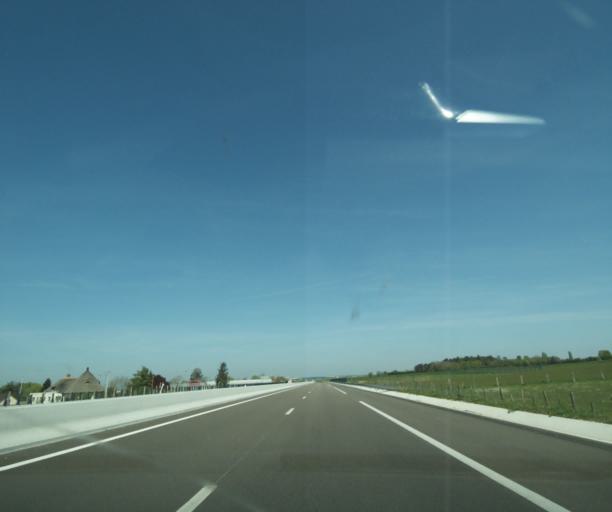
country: FR
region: Bourgogne
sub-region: Departement de la Nievre
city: Saint-Pierre-le-Moutier
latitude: 46.8113
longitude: 3.1225
